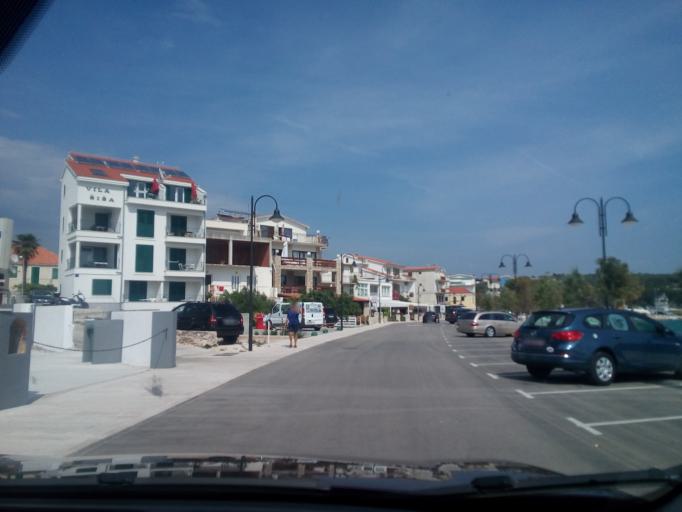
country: HR
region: Sibensko-Kniniska
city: Primosten
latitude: 43.5858
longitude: 15.9261
